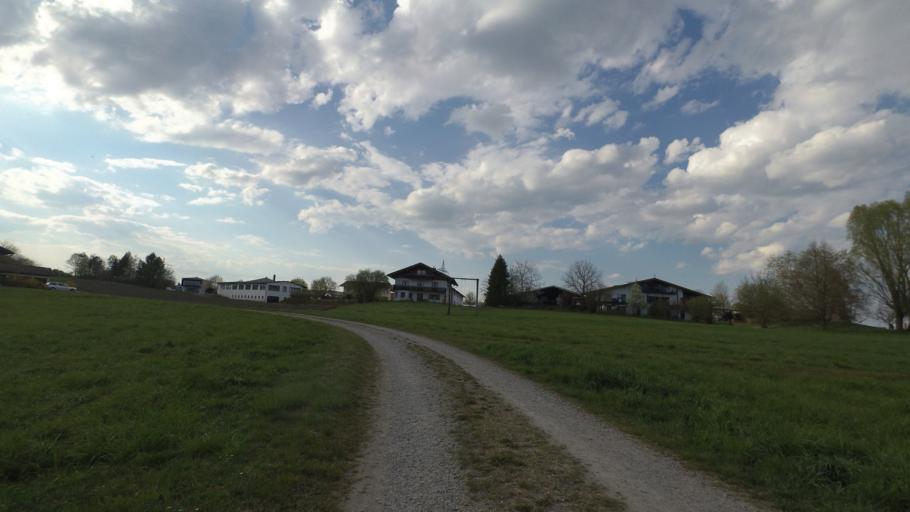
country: DE
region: Bavaria
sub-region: Upper Bavaria
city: Seeon-Seebruck
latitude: 47.9376
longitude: 12.4810
